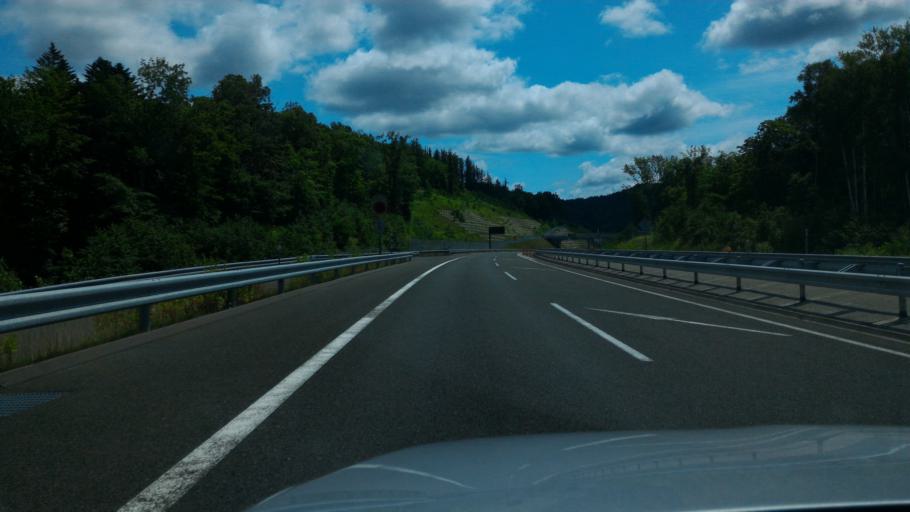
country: JP
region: Hokkaido
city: Shimo-furano
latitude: 42.9870
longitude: 142.4118
